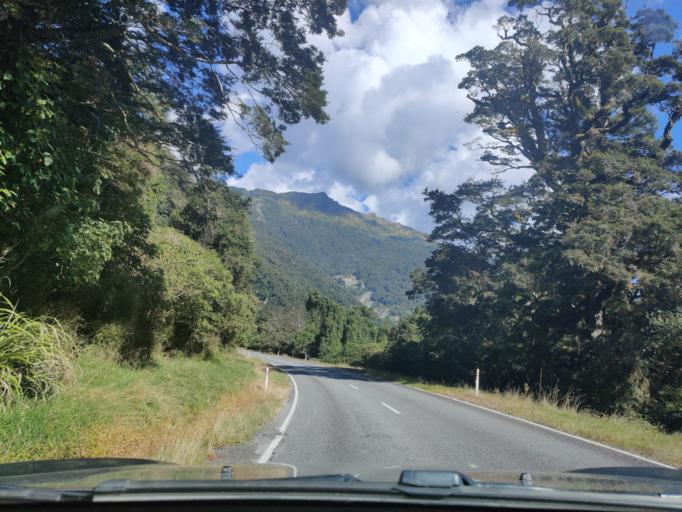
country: NZ
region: Otago
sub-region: Queenstown-Lakes District
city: Wanaka
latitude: -43.9698
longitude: 169.3992
